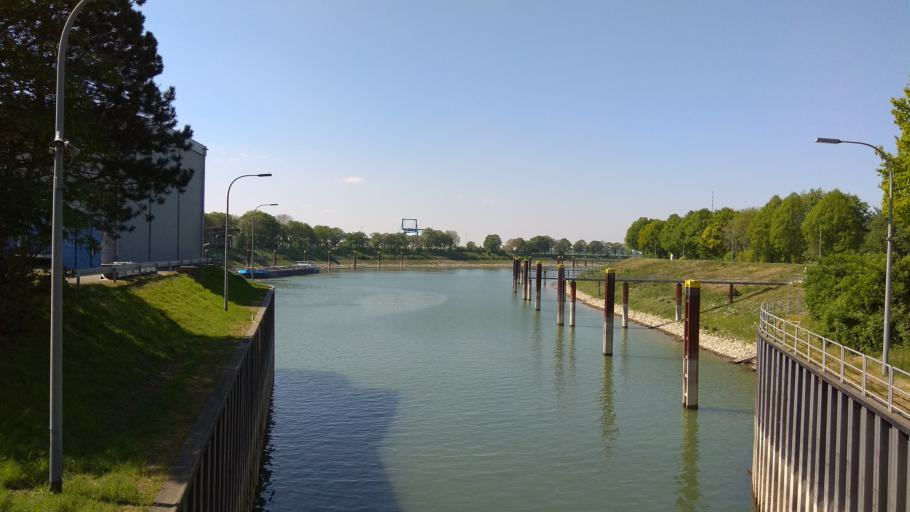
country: DE
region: North Rhine-Westphalia
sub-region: Regierungsbezirk Dusseldorf
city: Wesel
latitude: 51.6294
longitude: 6.6157
